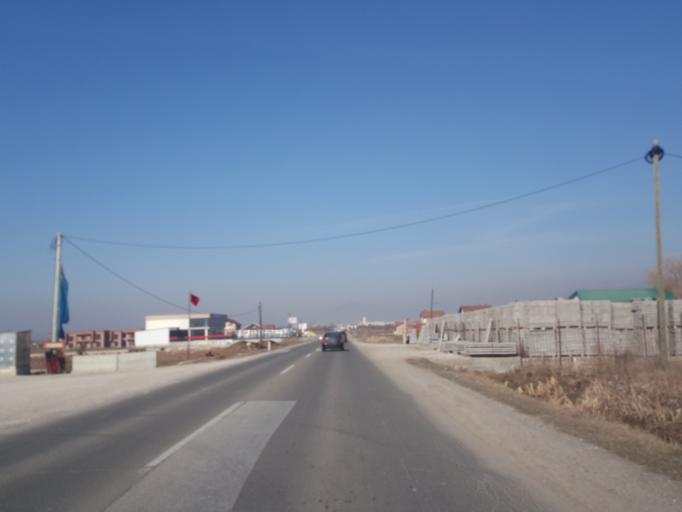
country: XK
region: Mitrovica
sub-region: Vushtrri
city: Vushtrri
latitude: 42.7914
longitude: 21.0040
